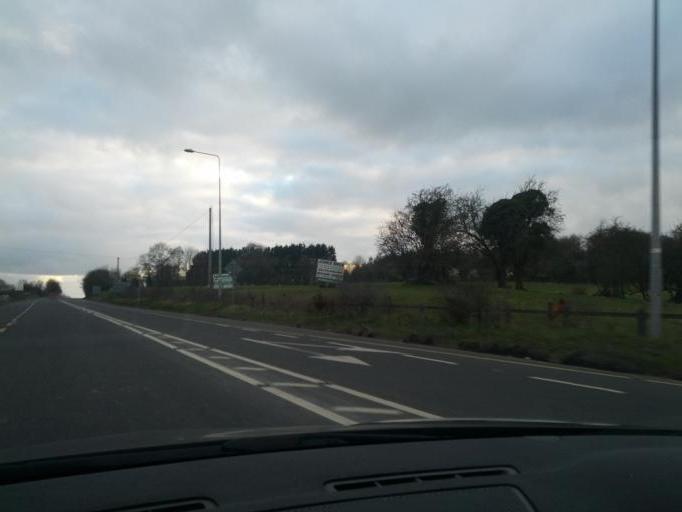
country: IE
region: Leinster
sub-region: Uibh Fhaili
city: Birr
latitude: 53.1169
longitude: -7.8906
